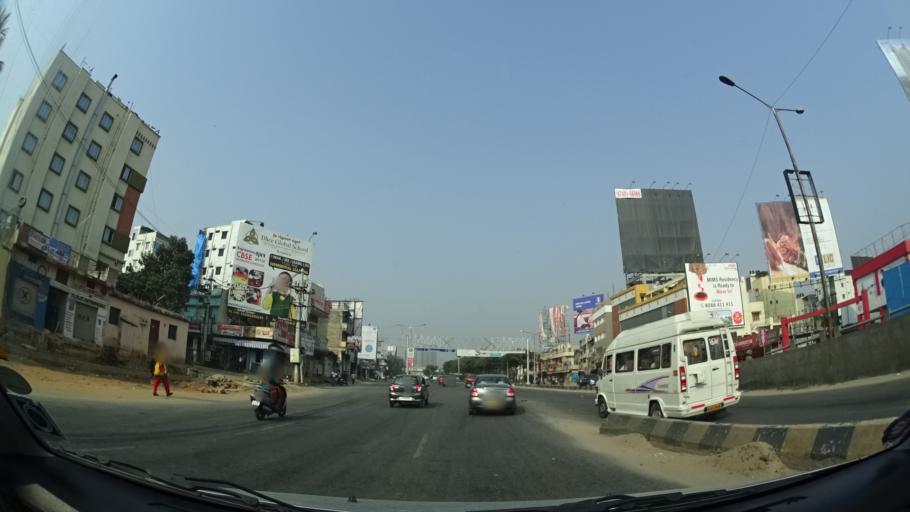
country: IN
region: Karnataka
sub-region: Bangalore Urban
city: Yelahanka
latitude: 13.0410
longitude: 77.6231
